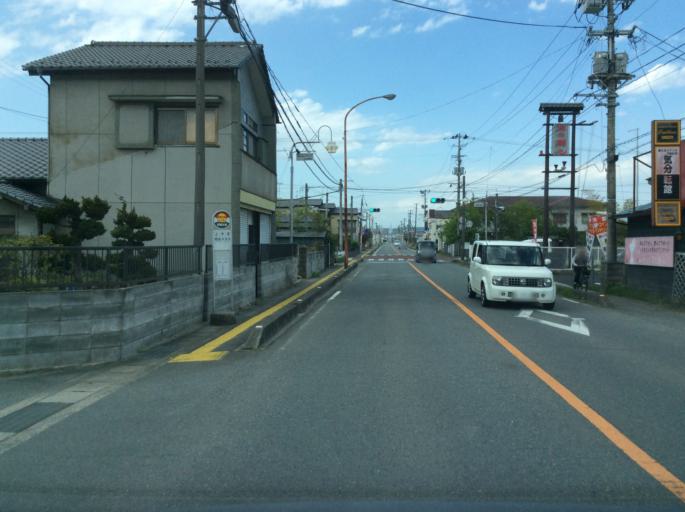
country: JP
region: Ibaraki
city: Kitaibaraki
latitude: 36.8988
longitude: 140.7850
